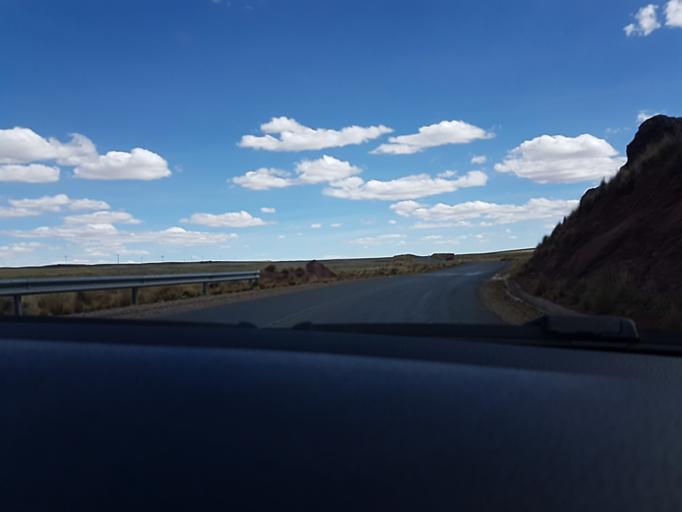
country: BO
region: La Paz
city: Tiahuanaco
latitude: -17.0288
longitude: -68.4367
